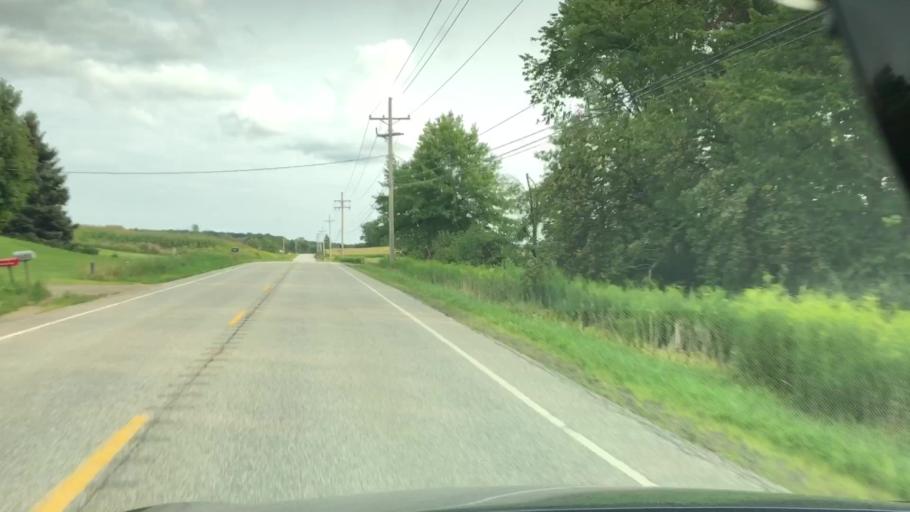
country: US
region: Pennsylvania
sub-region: Erie County
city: Union City
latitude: 41.9489
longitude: -79.8484
